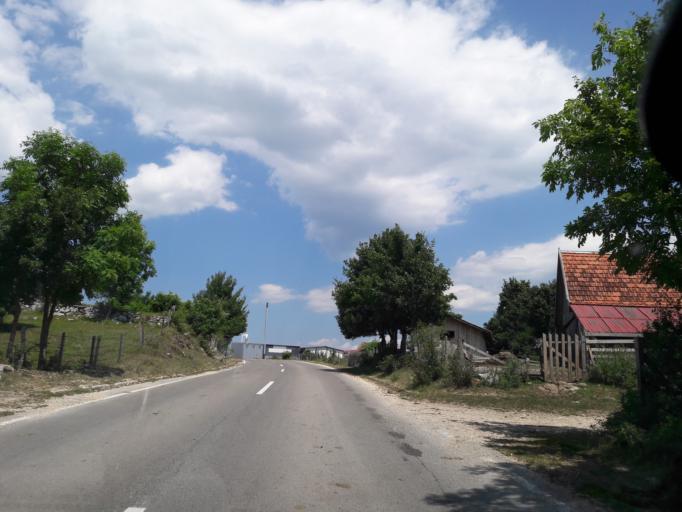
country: BA
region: Republika Srpska
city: Sipovo
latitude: 44.1552
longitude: 17.1686
